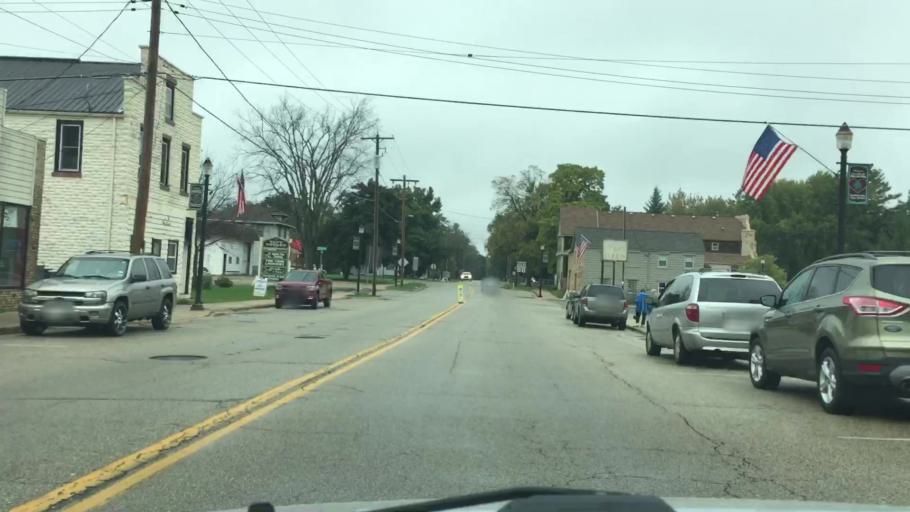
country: US
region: Wisconsin
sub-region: Jefferson County
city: Palmyra
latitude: 42.8781
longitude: -88.5857
